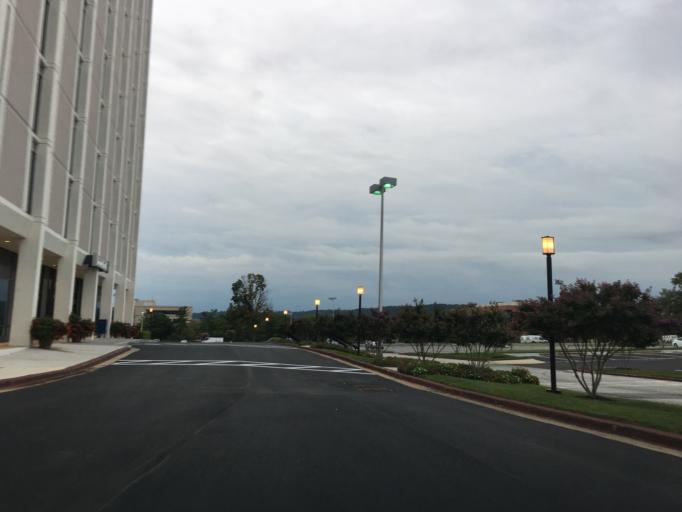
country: US
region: Maryland
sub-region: Baltimore County
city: Hunt Valley
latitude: 39.4941
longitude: -76.6614
